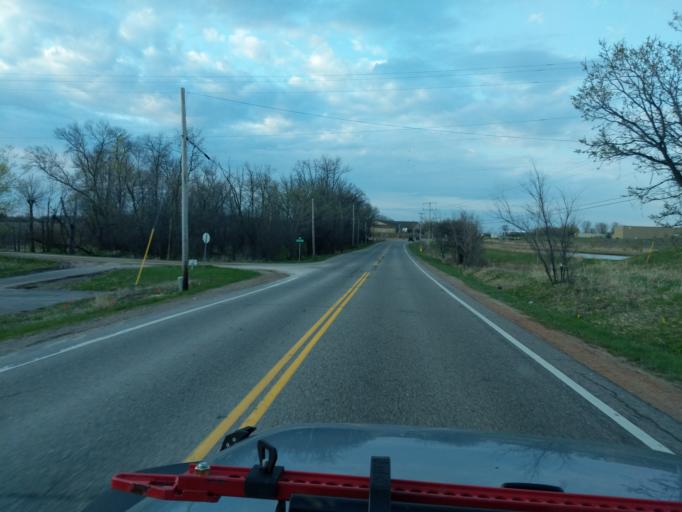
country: US
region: Minnesota
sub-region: Hennepin County
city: Rogers
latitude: 45.1796
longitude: -93.5224
